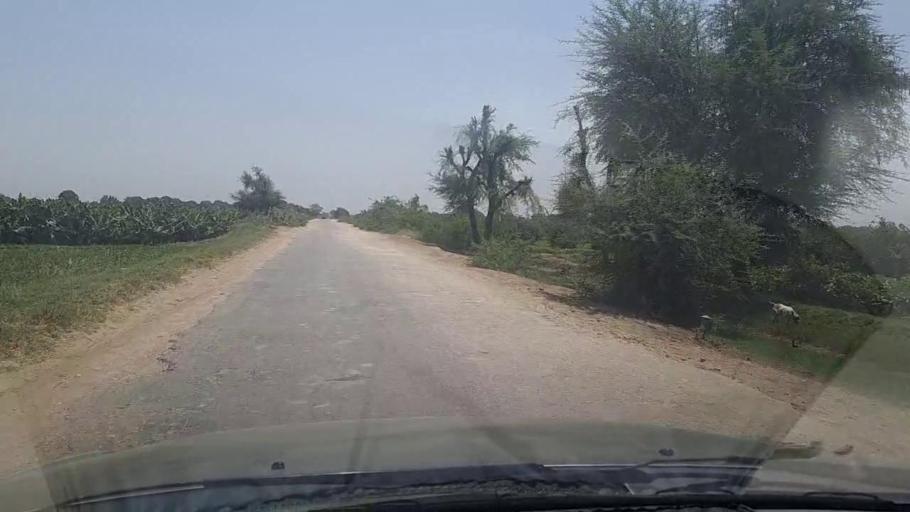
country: PK
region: Sindh
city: Tando Jam
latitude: 25.2760
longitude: 68.6206
